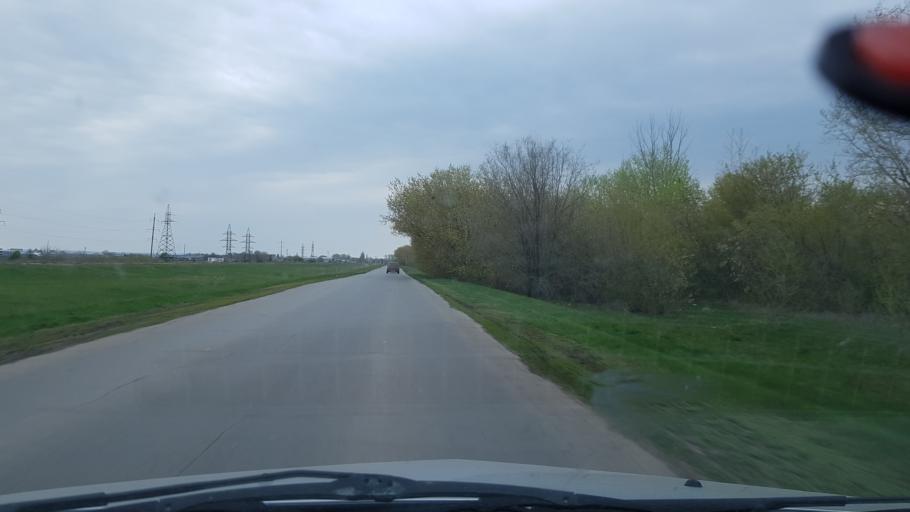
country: RU
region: Samara
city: Khryashchevka
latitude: 53.6714
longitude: 49.0986
